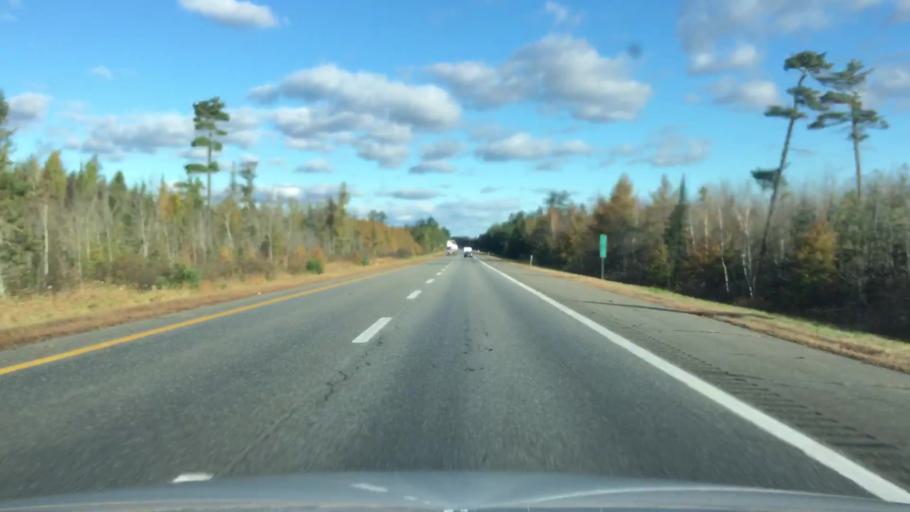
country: US
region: Maine
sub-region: Penobscot County
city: Greenbush
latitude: 45.1305
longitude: -68.6968
